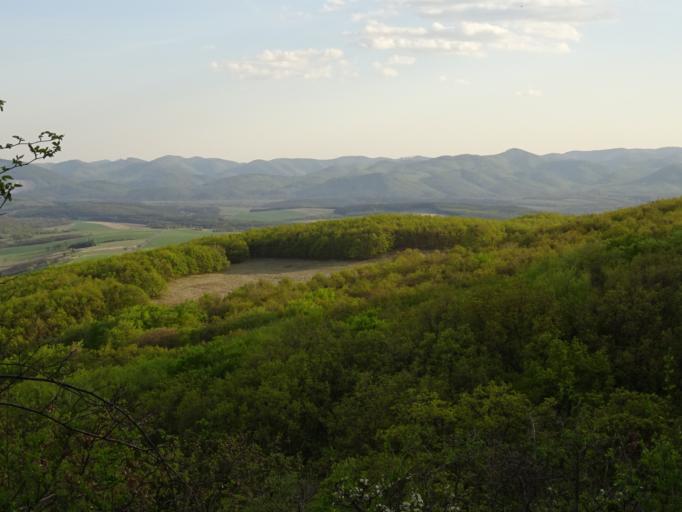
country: HU
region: Borsod-Abauj-Zemplen
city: Gonc
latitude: 48.5448
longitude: 21.4782
